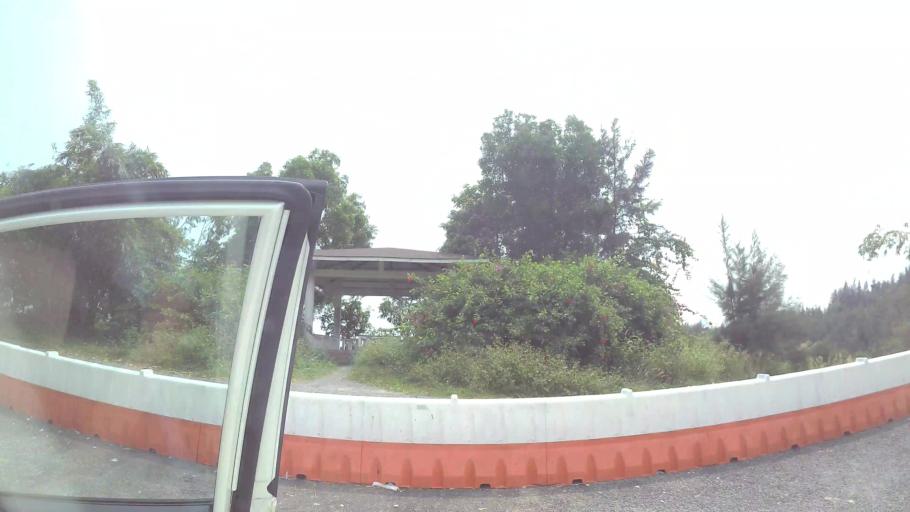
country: VN
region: Da Nang
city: Son Tra
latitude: 16.1002
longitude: 108.2715
